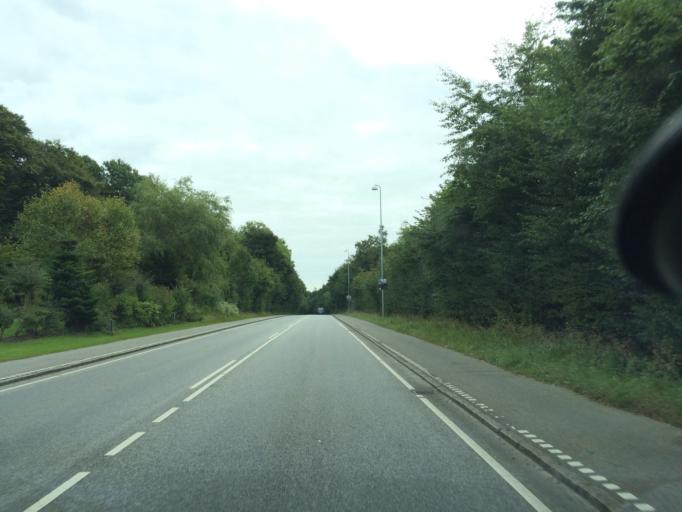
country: DK
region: South Denmark
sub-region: Aabenraa Kommune
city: Aabenraa
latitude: 55.0583
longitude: 9.3749
